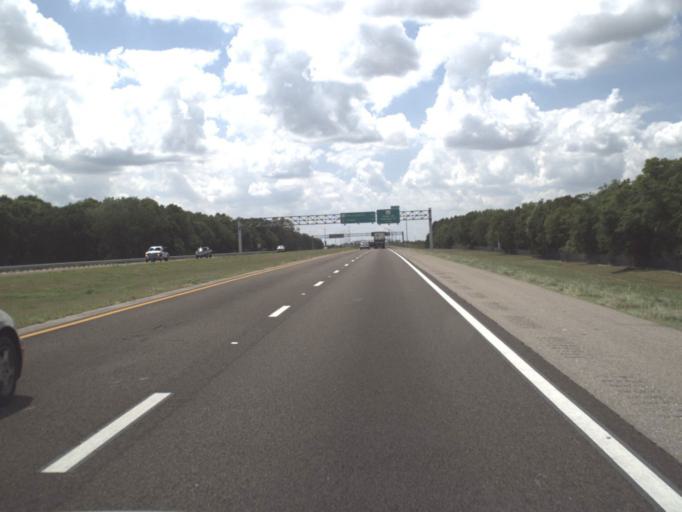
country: US
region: Florida
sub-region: Orange County
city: Ocoee
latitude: 28.5885
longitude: -81.5577
